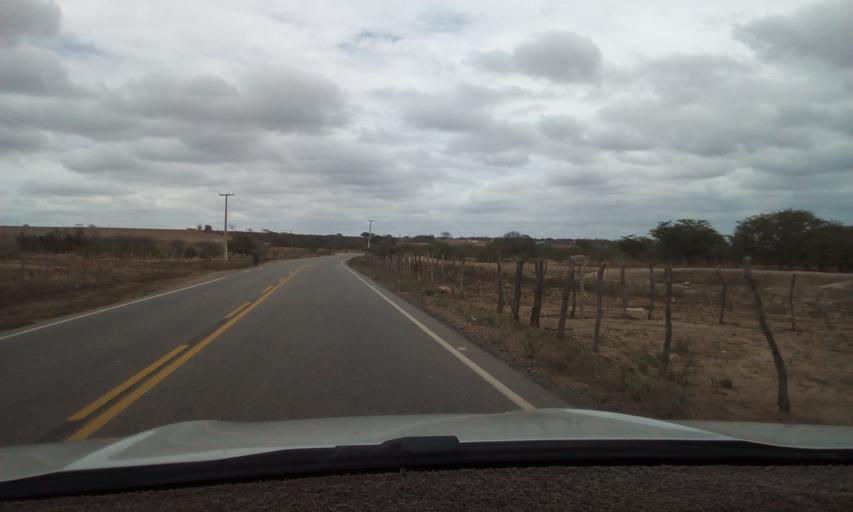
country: BR
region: Paraiba
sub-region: Picui
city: Picui
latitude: -6.5577
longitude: -36.2917
